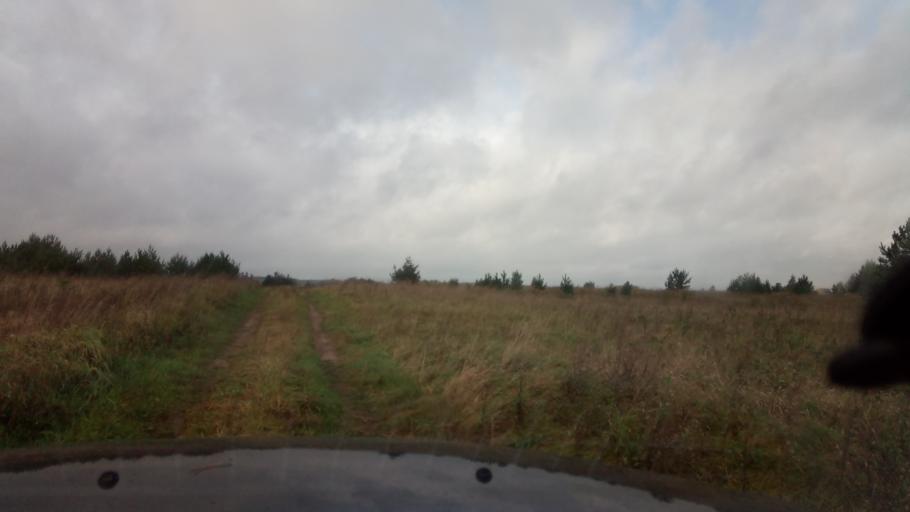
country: LT
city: Skaidiskes
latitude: 54.6193
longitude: 25.5176
